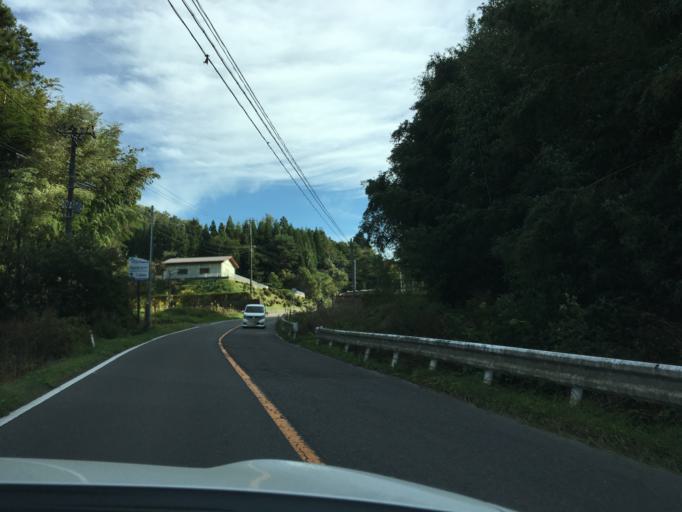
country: JP
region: Fukushima
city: Miharu
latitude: 37.3592
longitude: 140.4723
